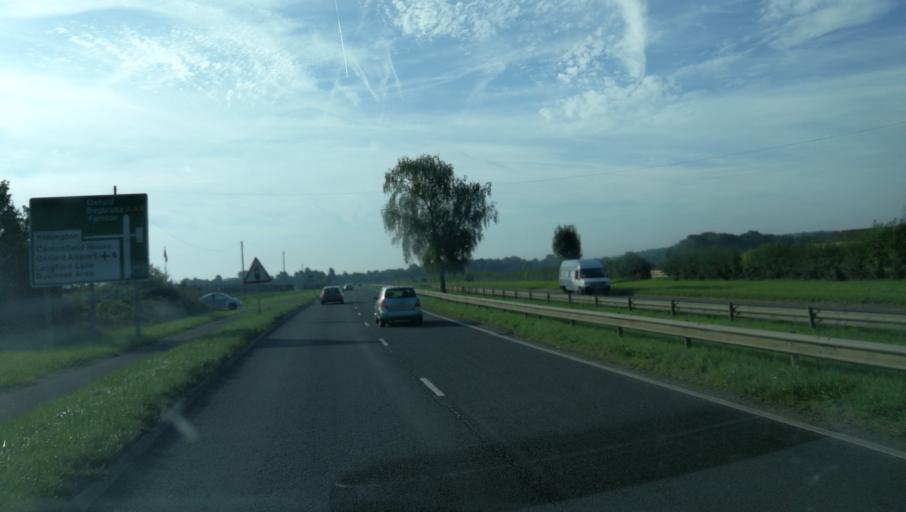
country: GB
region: England
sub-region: Oxfordshire
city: Yarnton
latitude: 51.8325
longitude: -1.3259
